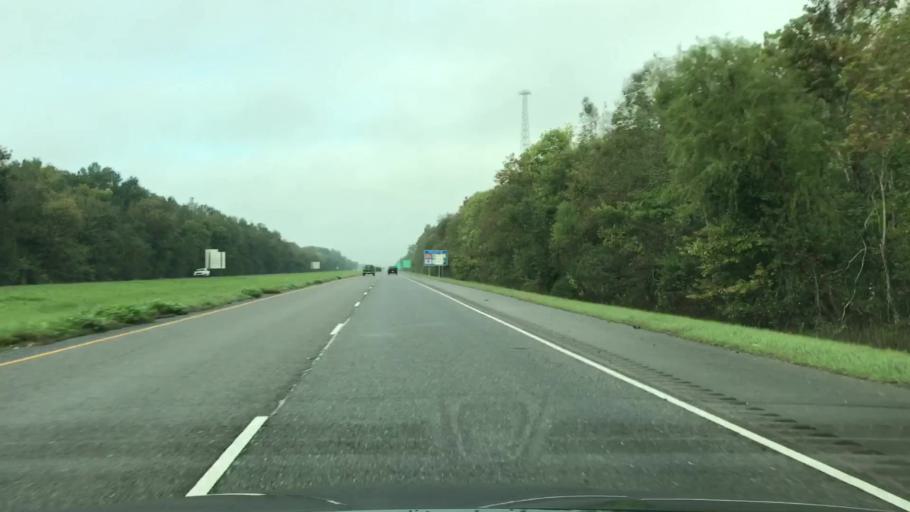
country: US
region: Louisiana
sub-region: Terrebonne Parish
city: Gray
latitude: 29.6816
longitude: -90.7636
